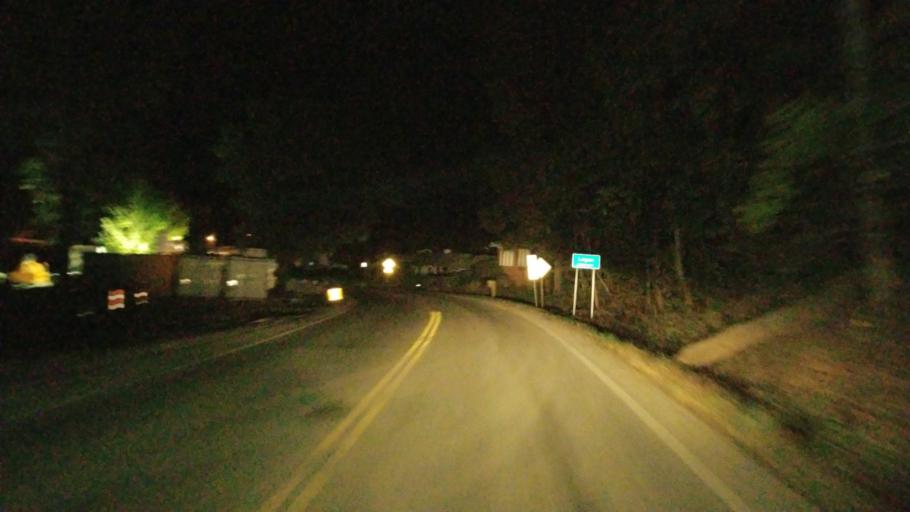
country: US
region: Ohio
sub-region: Hocking County
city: Logan
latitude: 39.5338
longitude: -82.4111
